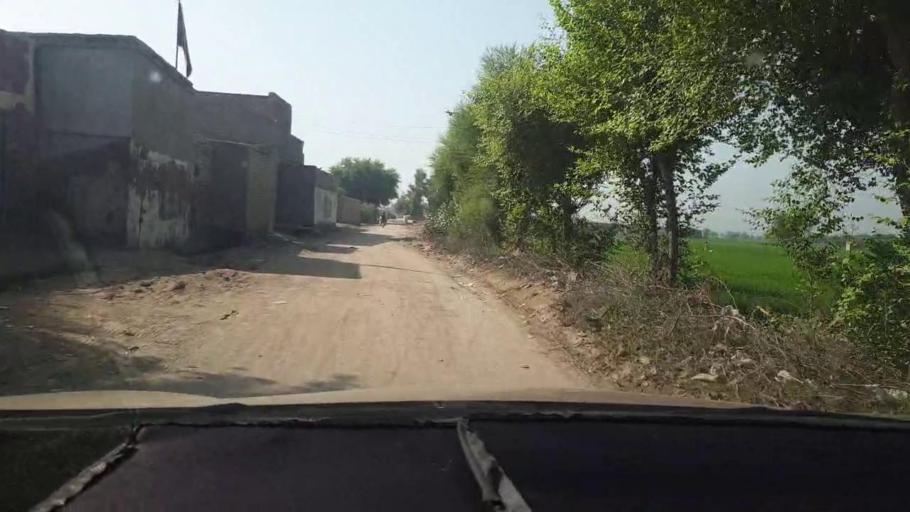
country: PK
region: Sindh
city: Kambar
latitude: 27.6045
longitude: 68.0927
